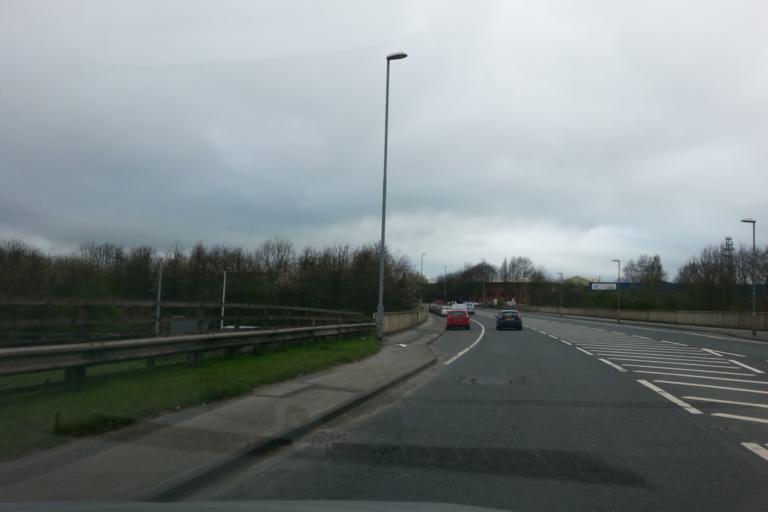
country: GB
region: England
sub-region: City and Borough of Leeds
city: Gildersome
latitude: 53.7454
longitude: -1.6246
